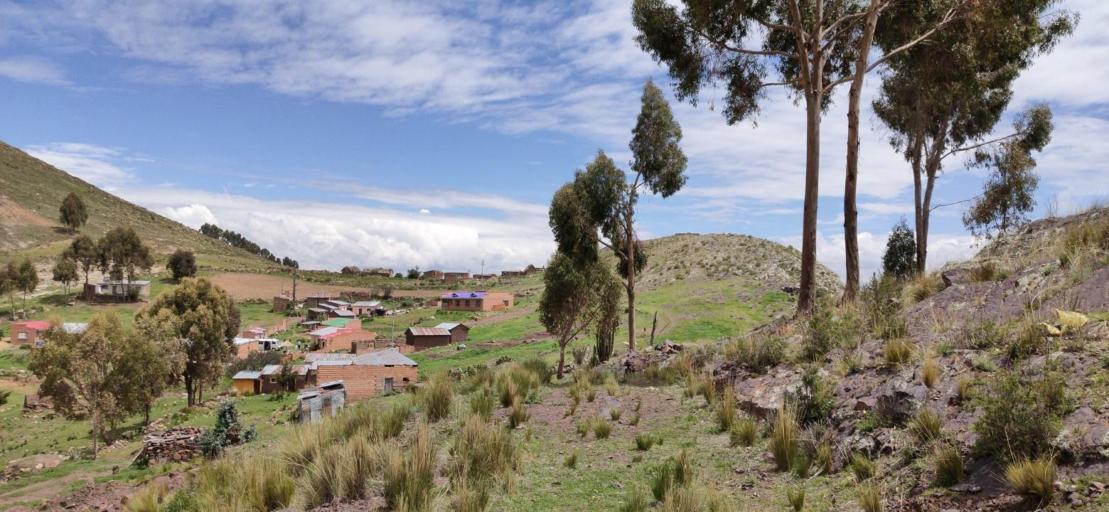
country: BO
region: La Paz
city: Batallas
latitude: -16.3459
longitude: -68.6363
